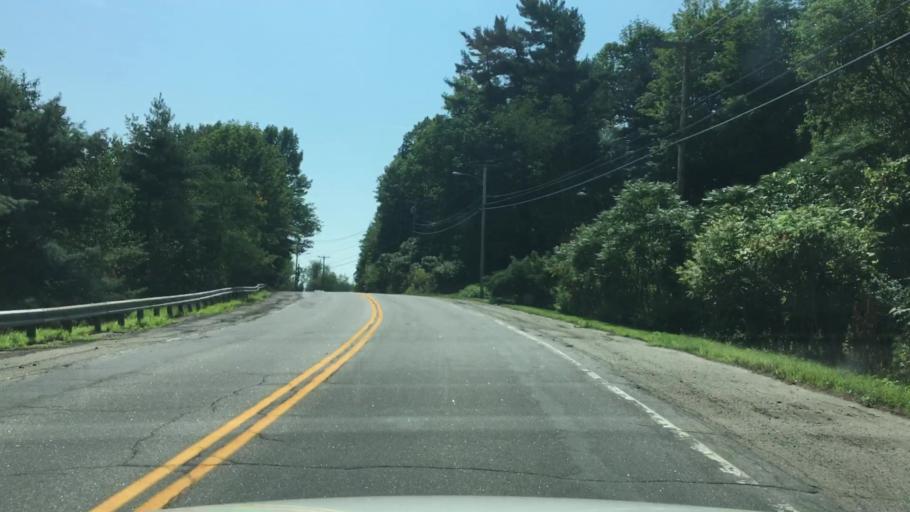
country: US
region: Maine
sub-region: Kennebec County
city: Hallowell
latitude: 44.2719
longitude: -69.7913
